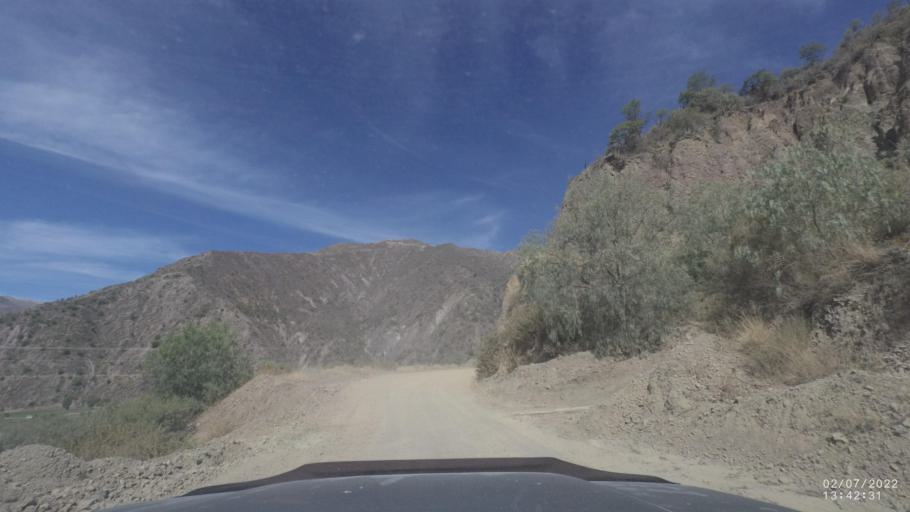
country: BO
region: Cochabamba
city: Irpa Irpa
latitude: -17.8004
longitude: -66.3561
